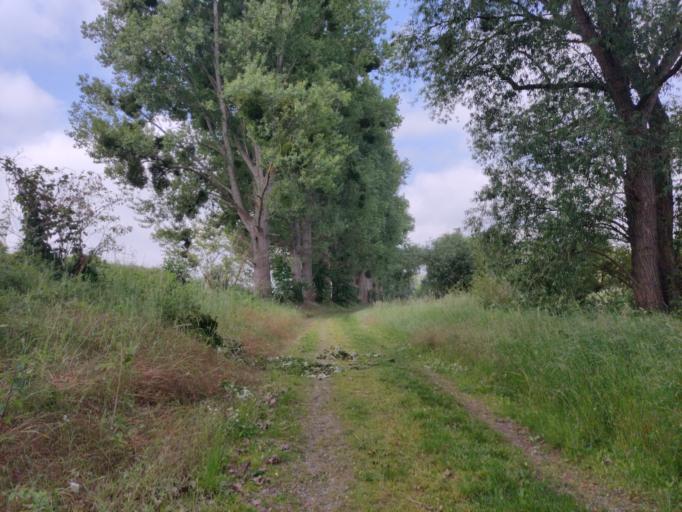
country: DE
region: Lower Saxony
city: Holle
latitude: 52.1005
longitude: 10.1174
